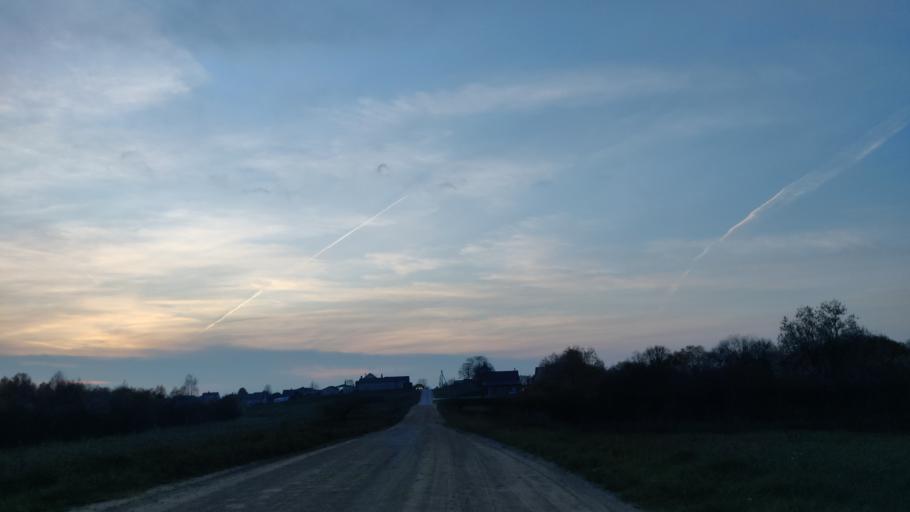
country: LT
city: Lentvaris
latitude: 54.5835
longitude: 25.0588
